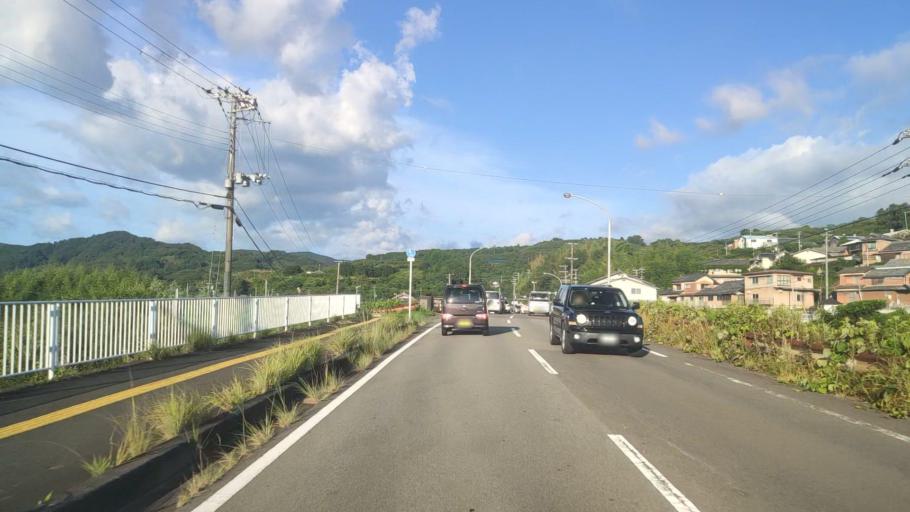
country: JP
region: Wakayama
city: Tanabe
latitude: 33.7347
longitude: 135.4255
